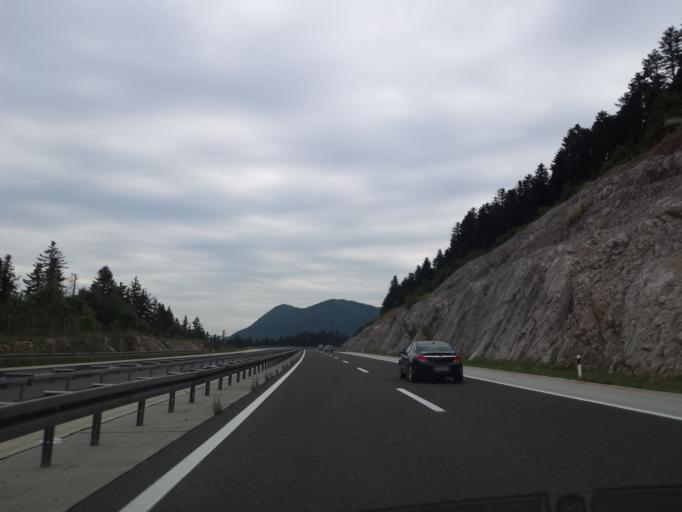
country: HR
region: Licko-Senjska
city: Otocac
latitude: 44.8325
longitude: 15.2552
